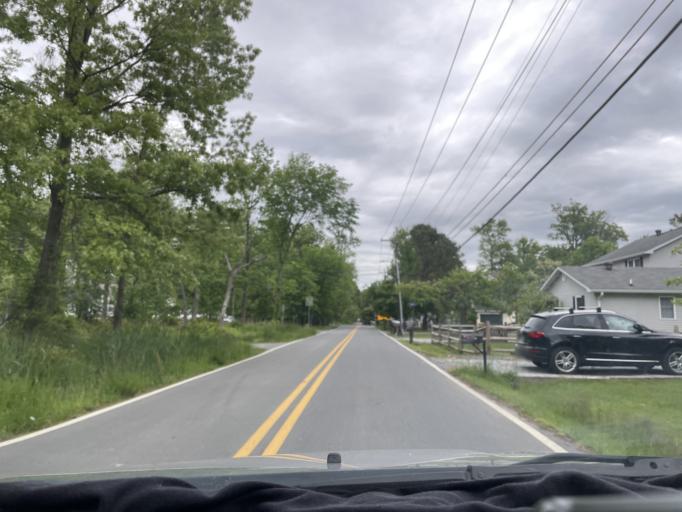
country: US
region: Maryland
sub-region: Calvert County
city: North Beach
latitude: 38.7153
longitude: -76.5290
